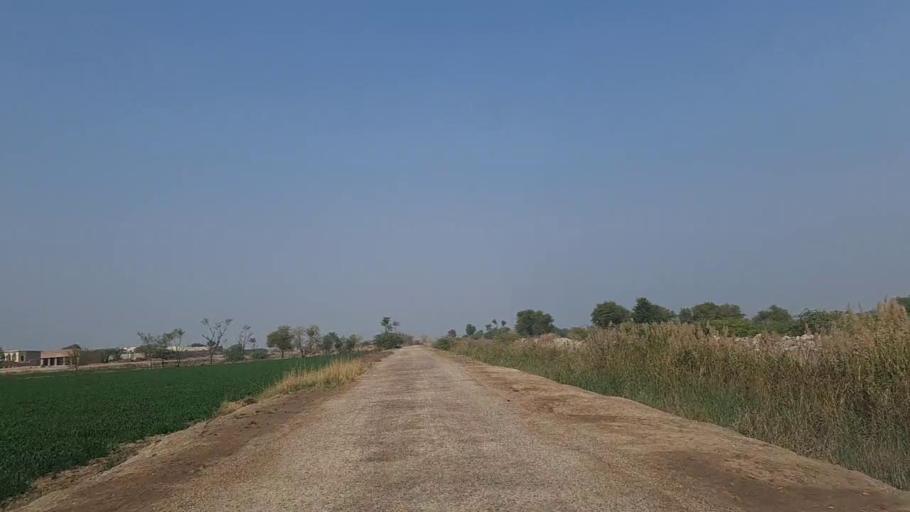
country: PK
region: Sindh
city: Nawabshah
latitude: 26.3682
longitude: 68.4260
